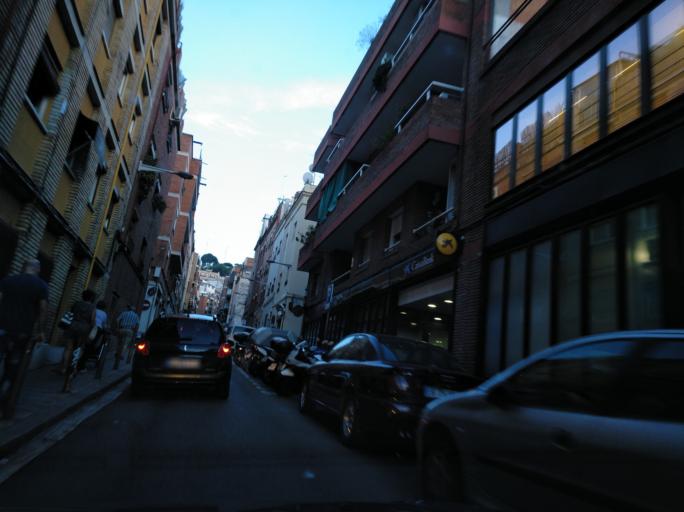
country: ES
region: Catalonia
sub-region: Provincia de Barcelona
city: Horta-Guinardo
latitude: 41.4228
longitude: 2.1561
